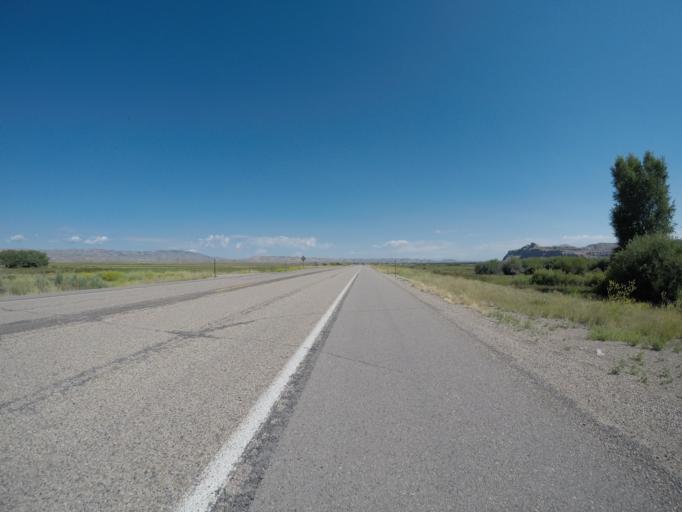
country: US
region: Wyoming
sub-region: Sublette County
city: Marbleton
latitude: 42.2287
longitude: -110.1924
